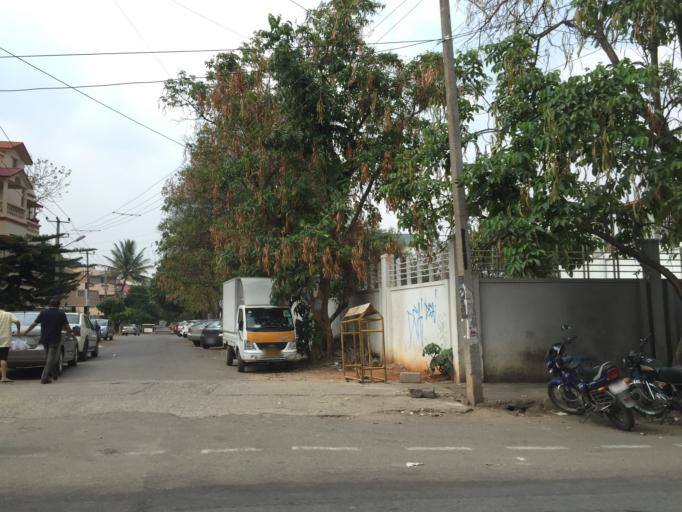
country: IN
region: Karnataka
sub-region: Bangalore Urban
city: Bangalore
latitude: 13.0213
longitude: 77.6421
